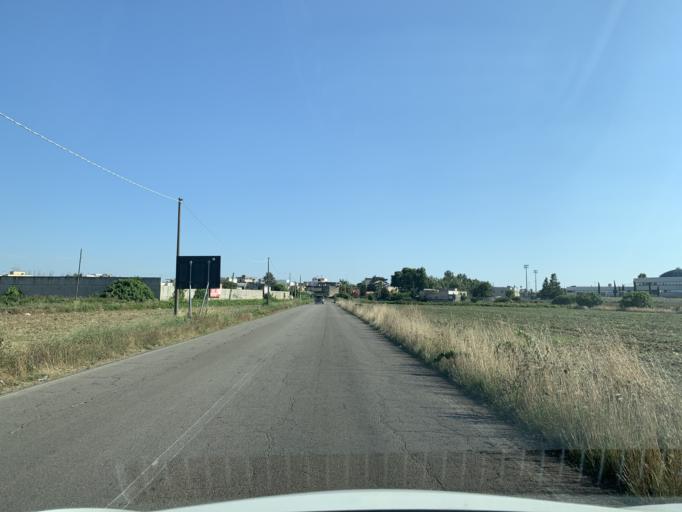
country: IT
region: Apulia
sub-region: Provincia di Lecce
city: Nardo
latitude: 40.1874
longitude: 18.0392
